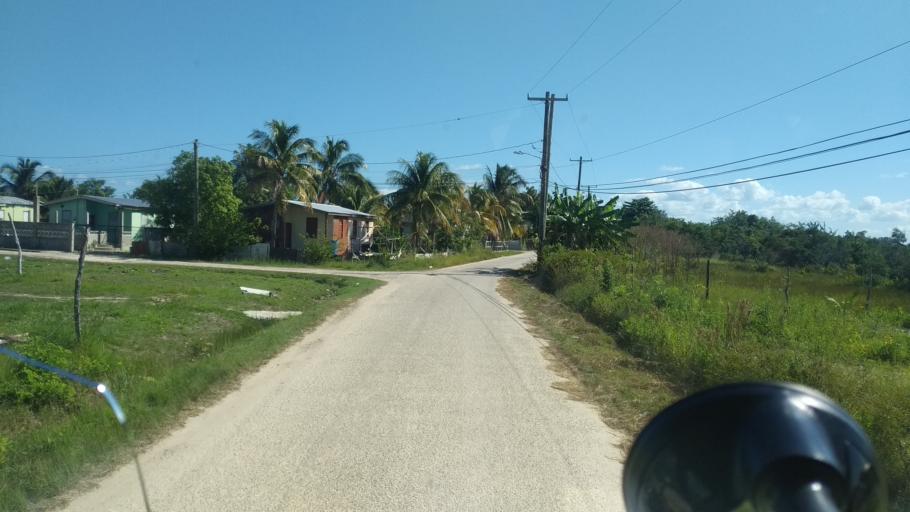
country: BZ
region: Belize
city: Belize City
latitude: 17.5609
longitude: -88.3030
